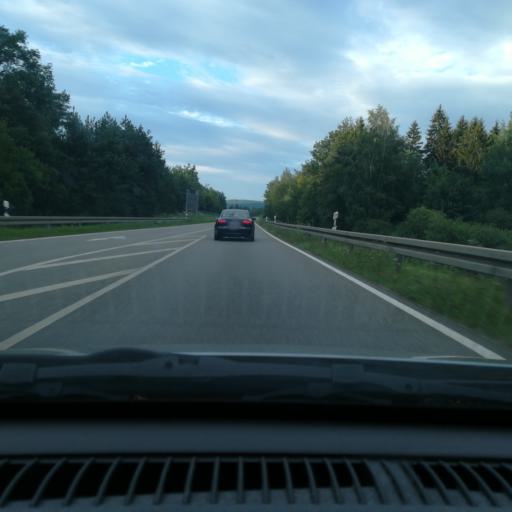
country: DE
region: Baden-Wuerttemberg
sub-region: Freiburg Region
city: Moos
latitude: 47.7608
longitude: 8.9066
